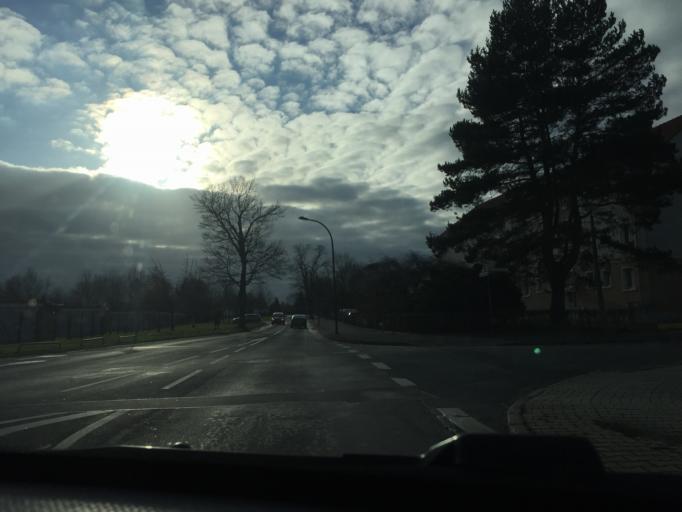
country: DE
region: Saxony
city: Goerlitz
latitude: 51.1436
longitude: 14.9482
